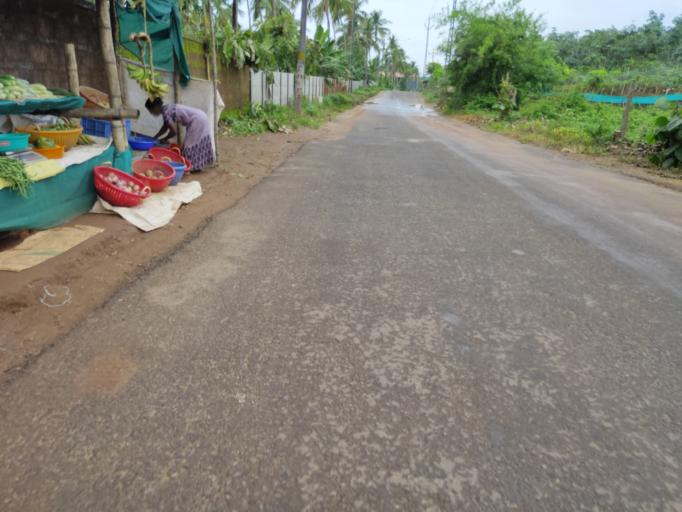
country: IN
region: Kerala
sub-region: Malappuram
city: Manjeri
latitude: 11.2306
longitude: 76.2799
